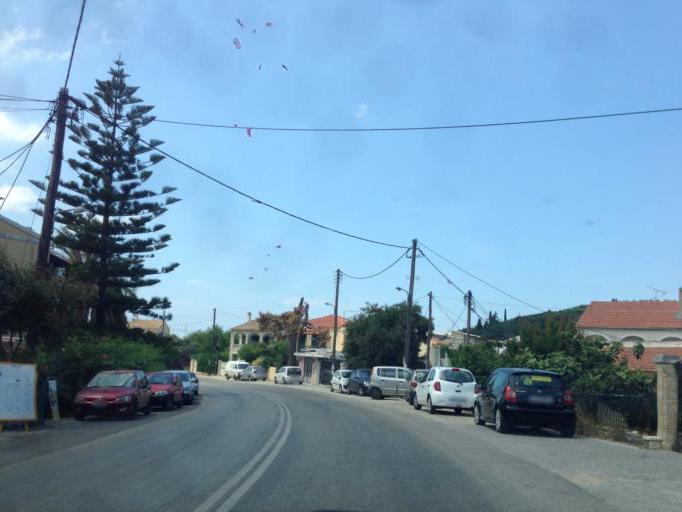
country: GR
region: Ionian Islands
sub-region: Nomos Kerkyras
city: Acharavi
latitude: 39.7874
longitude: 19.9197
